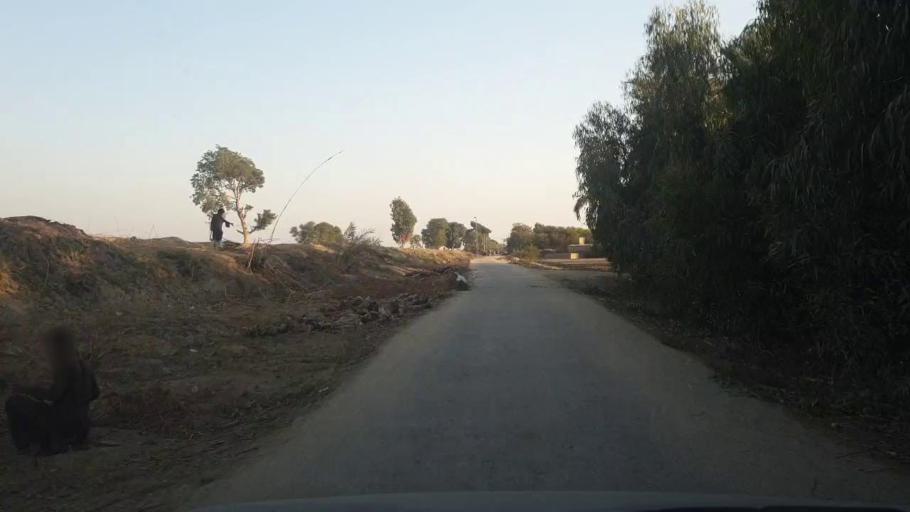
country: PK
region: Sindh
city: Chambar
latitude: 25.2900
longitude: 68.8953
